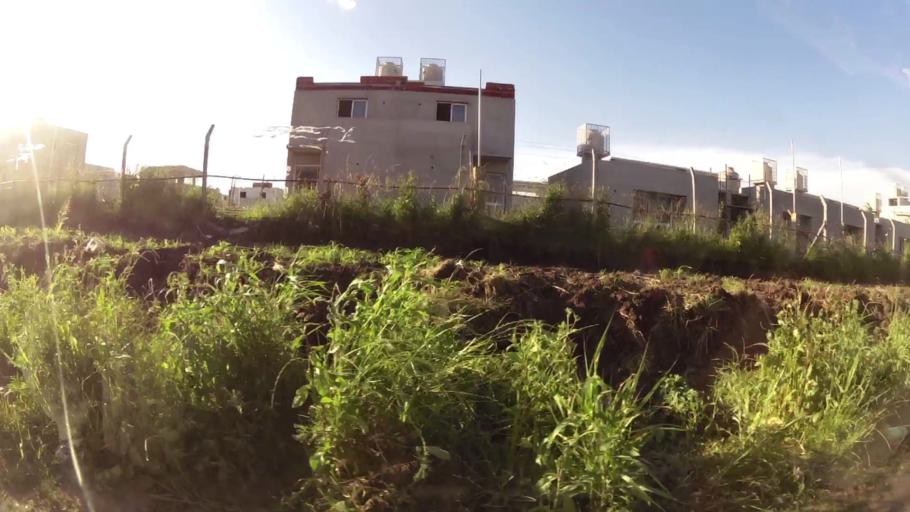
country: AR
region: Buenos Aires
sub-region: Partido de Merlo
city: Merlo
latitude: -34.6888
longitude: -58.7425
